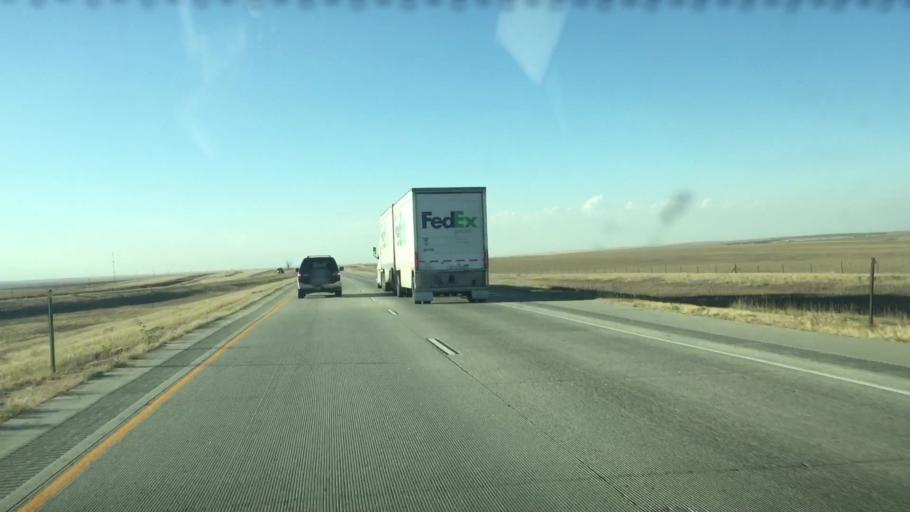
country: US
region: Colorado
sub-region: Lincoln County
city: Limon
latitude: 39.4209
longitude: -103.9090
